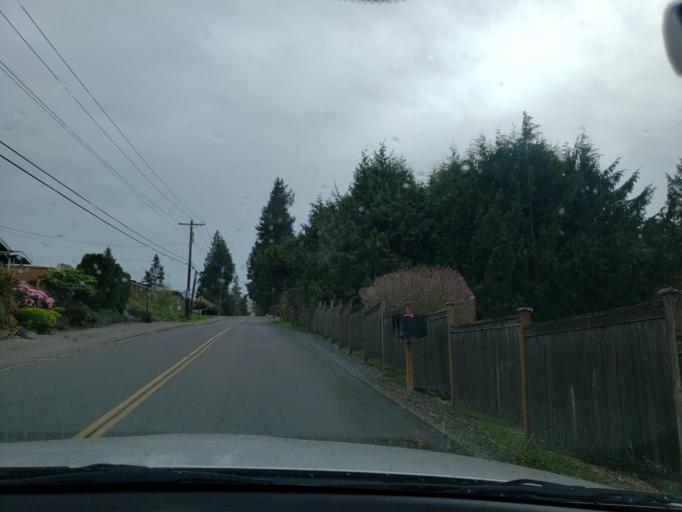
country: US
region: Washington
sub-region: Snohomish County
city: Meadowdale
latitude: 47.8346
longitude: -122.3522
